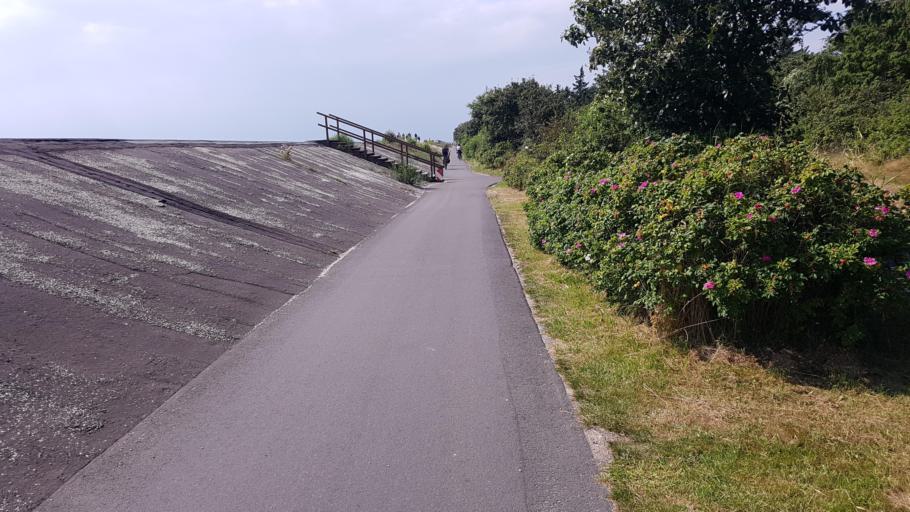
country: DE
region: Schleswig-Holstein
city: Sankt Peter-Ording
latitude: 54.3057
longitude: 8.6205
